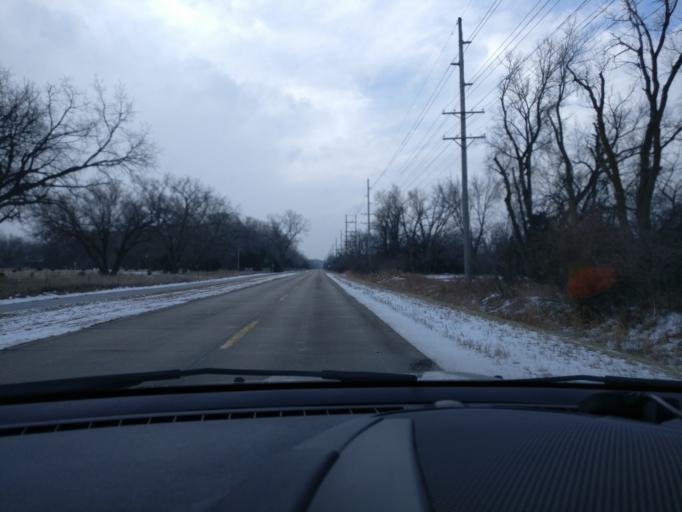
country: US
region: Nebraska
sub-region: Dodge County
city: Fremont
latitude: 41.4313
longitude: -96.5215
